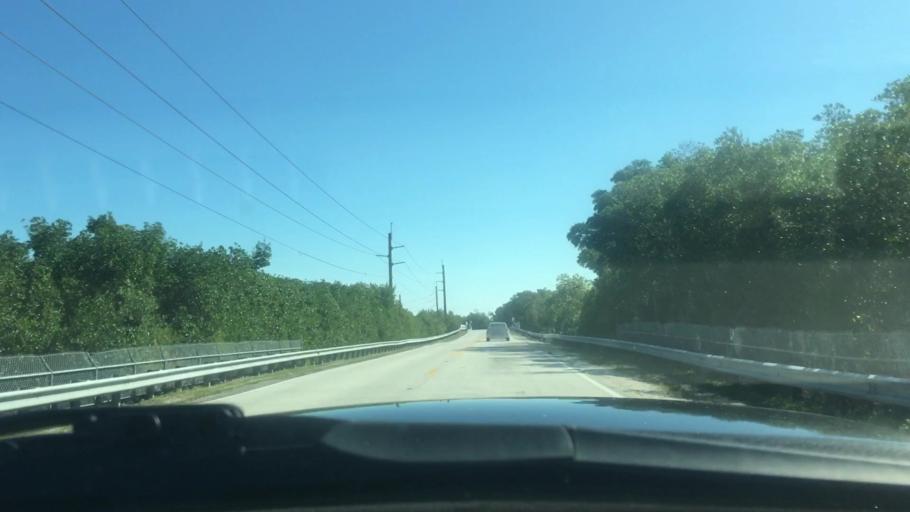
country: US
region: Florida
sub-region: Monroe County
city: North Key Largo
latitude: 25.2800
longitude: -80.3448
